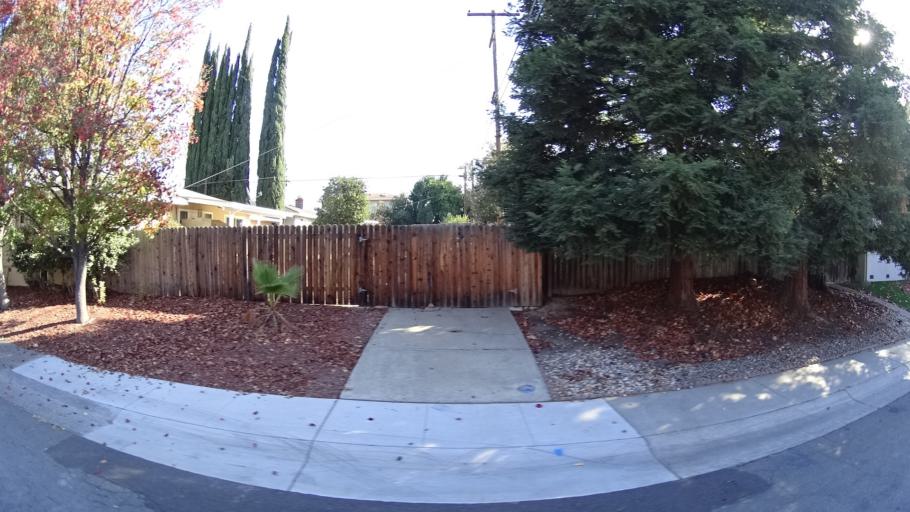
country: US
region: California
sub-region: Sacramento County
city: Antelope
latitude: 38.6792
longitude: -121.3079
